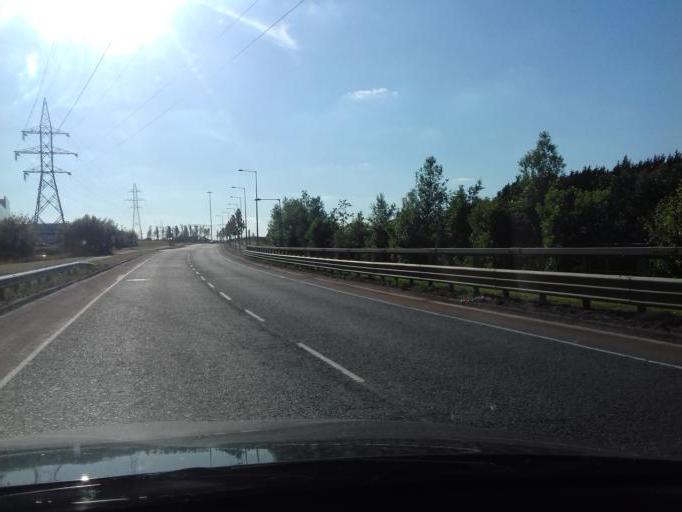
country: IE
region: Leinster
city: Hartstown
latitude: 53.4132
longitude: -6.4044
